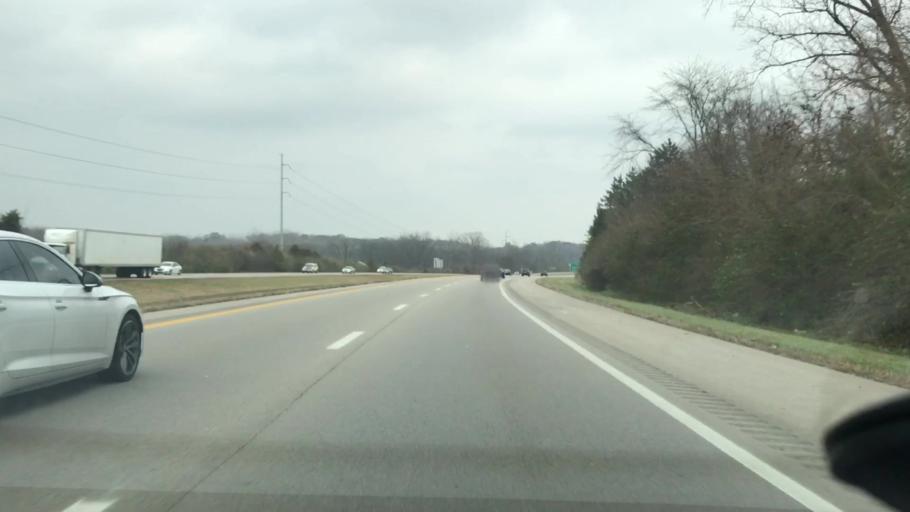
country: US
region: Ohio
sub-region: Greene County
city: Wright-Patterson AFB
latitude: 39.7763
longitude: -84.0374
